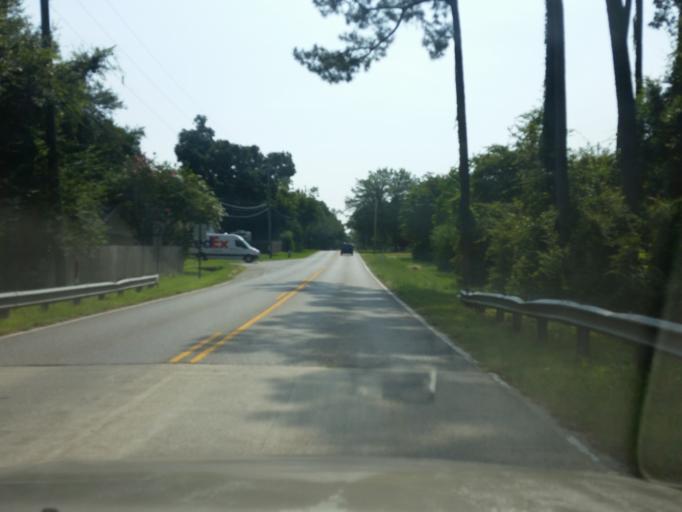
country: US
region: Florida
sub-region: Escambia County
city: Ensley
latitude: 30.5195
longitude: -87.3064
